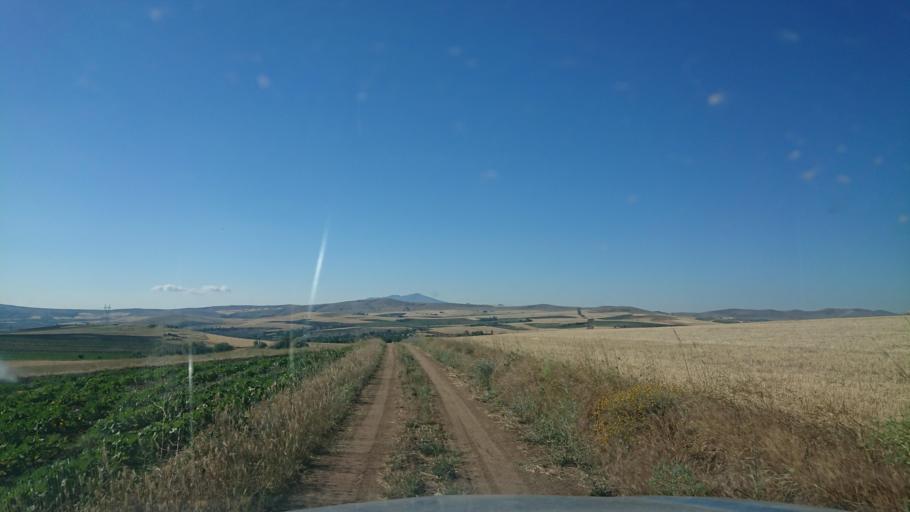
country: TR
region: Aksaray
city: Agacoren
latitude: 38.8358
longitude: 33.9382
